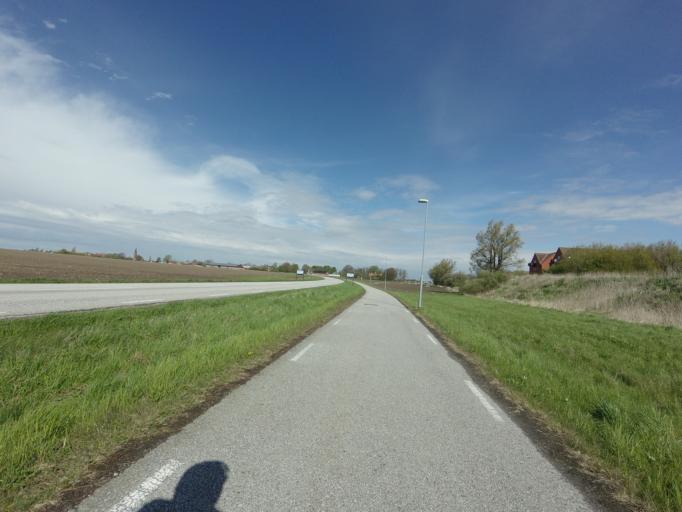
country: SE
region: Skane
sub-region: Malmo
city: Tygelsjo
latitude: 55.4973
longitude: 13.0003
